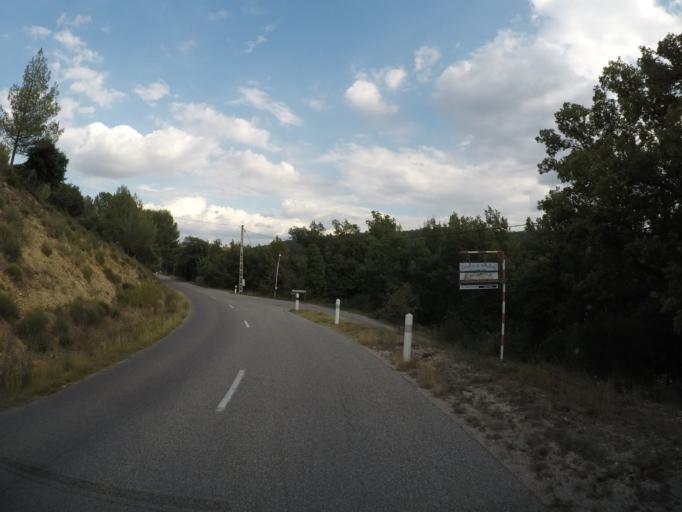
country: FR
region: Provence-Alpes-Cote d'Azur
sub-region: Departement des Alpes-de-Haute-Provence
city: Riez
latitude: 43.8121
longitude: 6.0581
